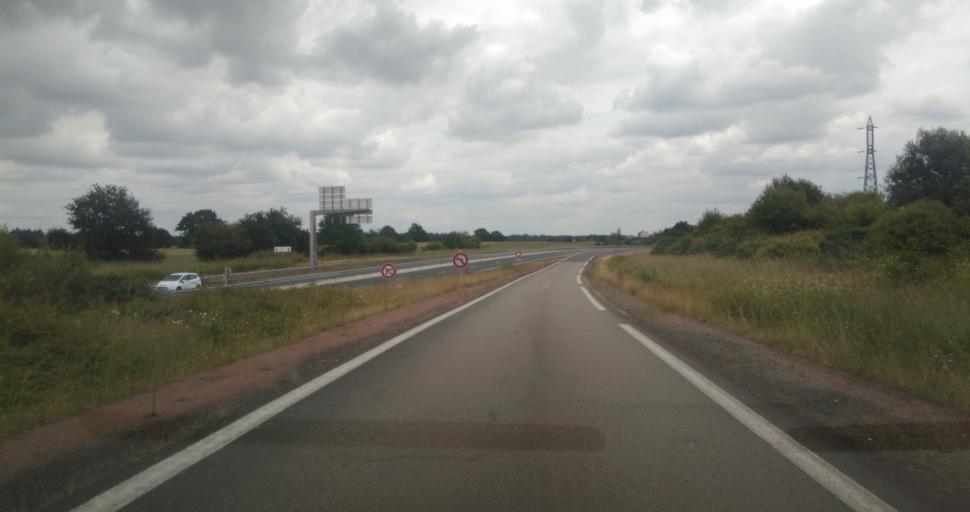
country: FR
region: Pays de la Loire
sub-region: Departement de la Vendee
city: La Chaize-le-Vicomte
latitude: 46.6628
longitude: -1.2660
